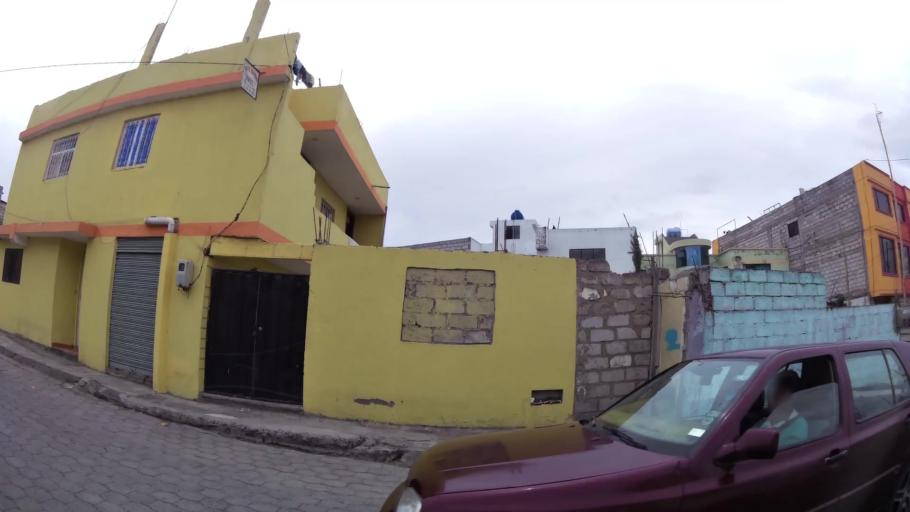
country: EC
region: Cotopaxi
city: San Miguel de Salcedo
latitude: -1.0471
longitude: -78.5861
